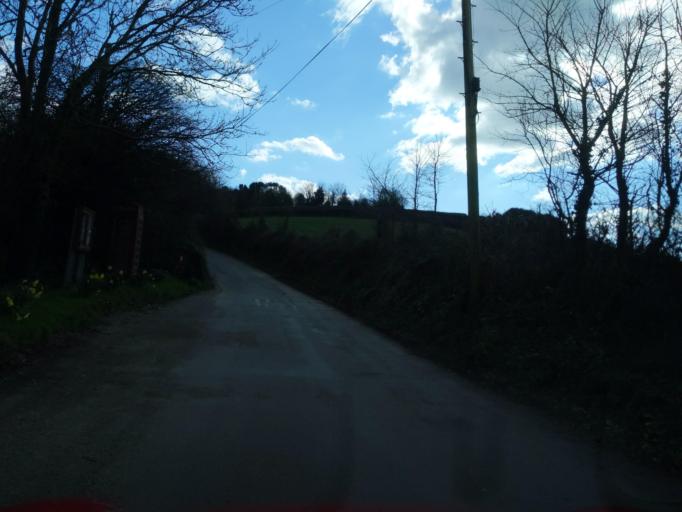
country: GB
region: England
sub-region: Devon
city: Salcombe
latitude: 50.2523
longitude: -3.7014
